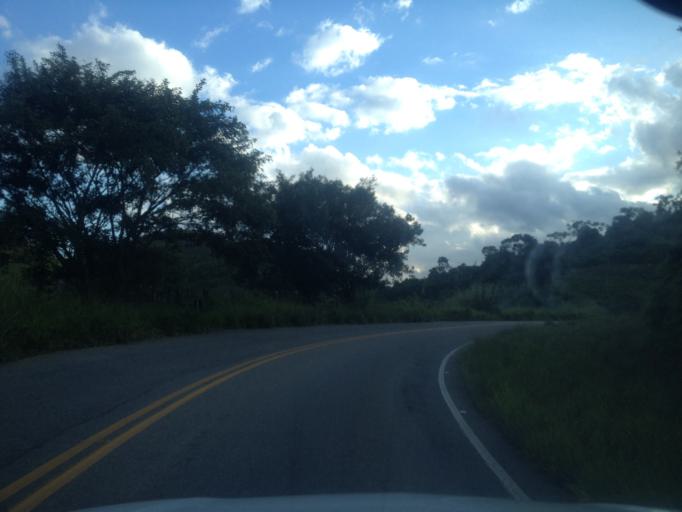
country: BR
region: Rio de Janeiro
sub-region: Quatis
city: Quatis
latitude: -22.3676
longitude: -44.2584
